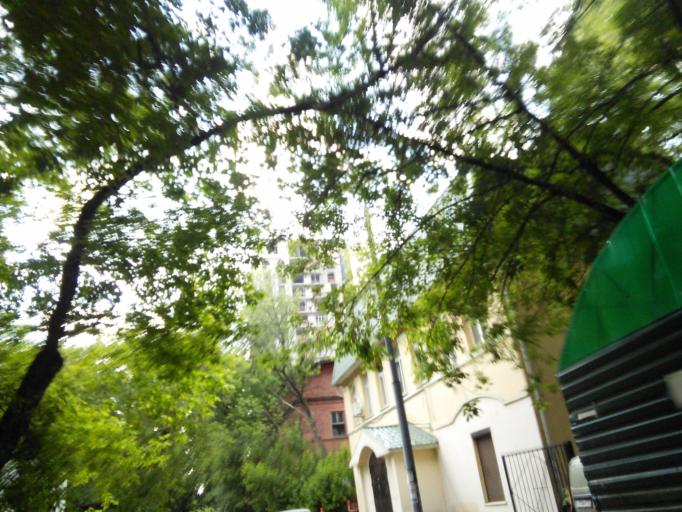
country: RU
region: Moskovskaya
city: Bogorodskoye
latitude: 55.8162
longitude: 37.7048
